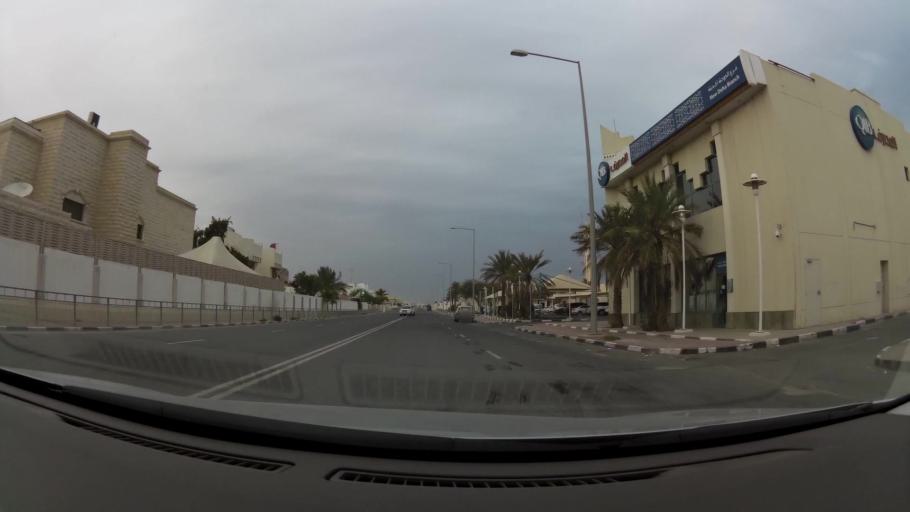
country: QA
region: Baladiyat ad Dawhah
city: Doha
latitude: 25.3311
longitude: 51.5108
